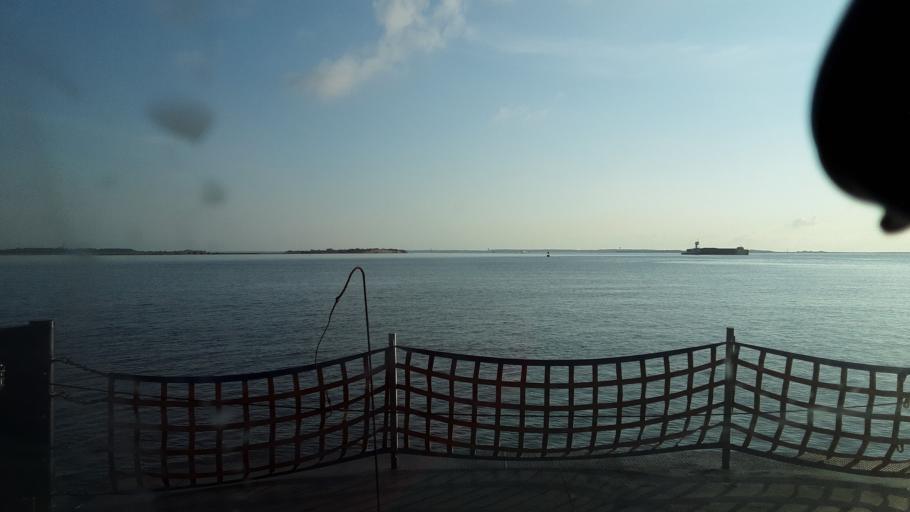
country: US
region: North Carolina
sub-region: Brunswick County
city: Southport
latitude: 33.9427
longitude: -77.9746
